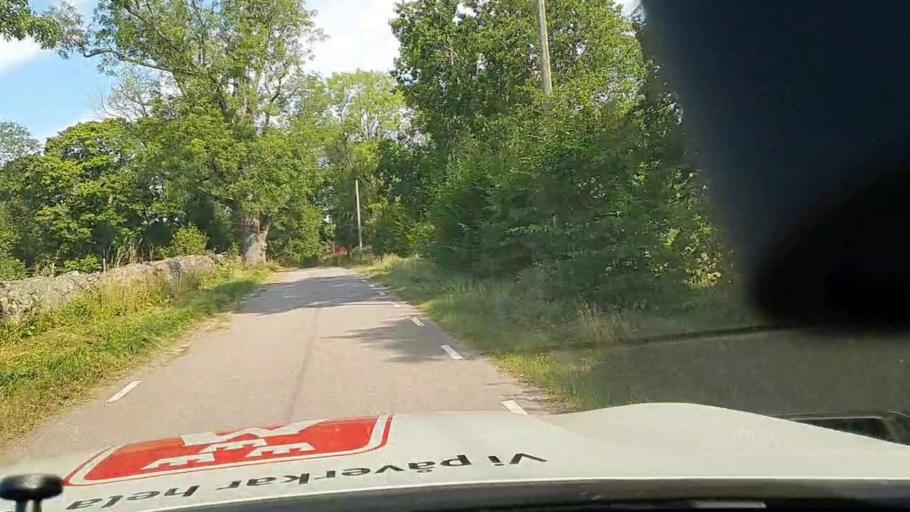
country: SE
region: Soedermanland
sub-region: Strangnas Kommun
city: Akers Styckebruk
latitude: 59.2711
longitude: 16.9823
